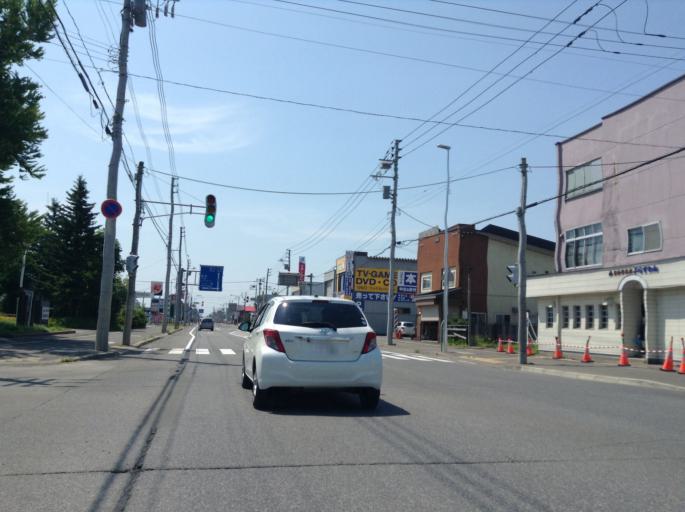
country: JP
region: Hokkaido
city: Nayoro
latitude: 44.3579
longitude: 142.4572
